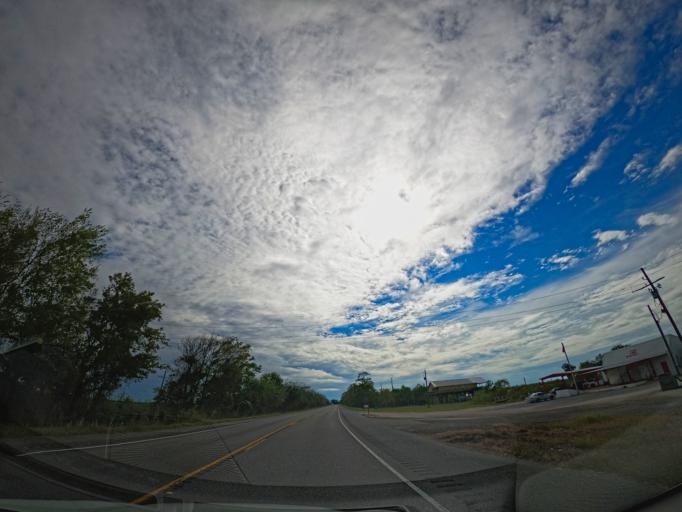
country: US
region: Louisiana
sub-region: Saint Tammany Parish
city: Eden Isle
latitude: 30.0790
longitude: -89.7923
